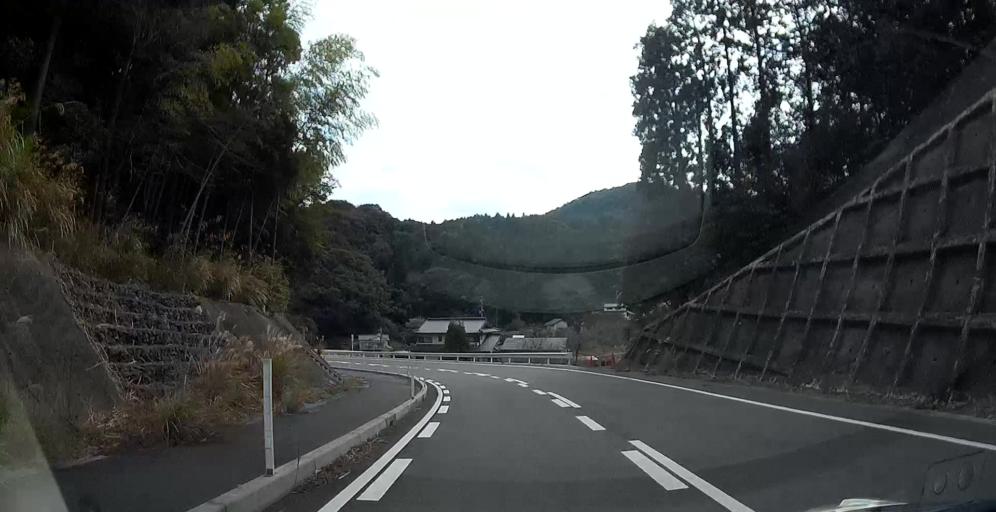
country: JP
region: Kumamoto
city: Minamata
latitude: 32.2312
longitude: 130.4268
